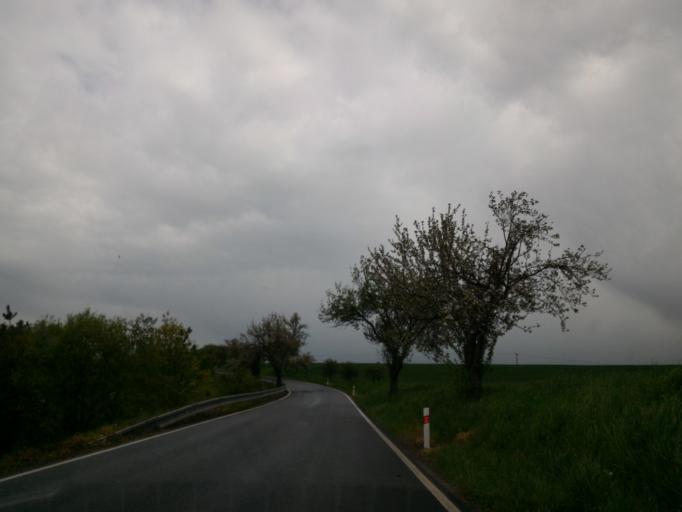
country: CZ
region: Vysocina
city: Ledec nad Sazavou
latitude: 49.7051
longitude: 15.2714
